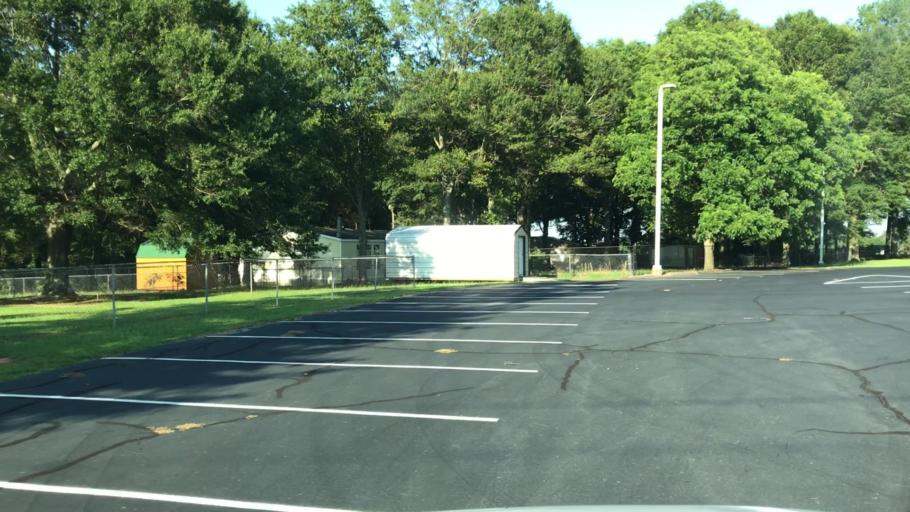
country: US
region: South Carolina
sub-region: Anderson County
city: Piedmont
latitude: 34.6645
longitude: -82.3934
